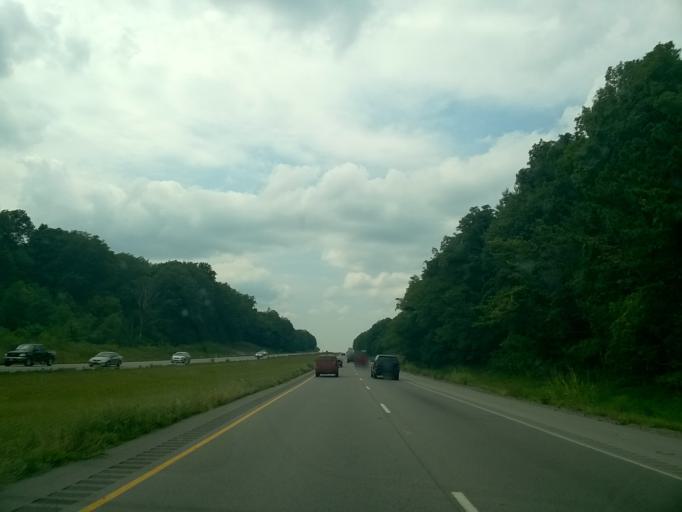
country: US
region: Indiana
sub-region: Putnam County
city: Cloverdale
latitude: 39.5331
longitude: -86.8241
